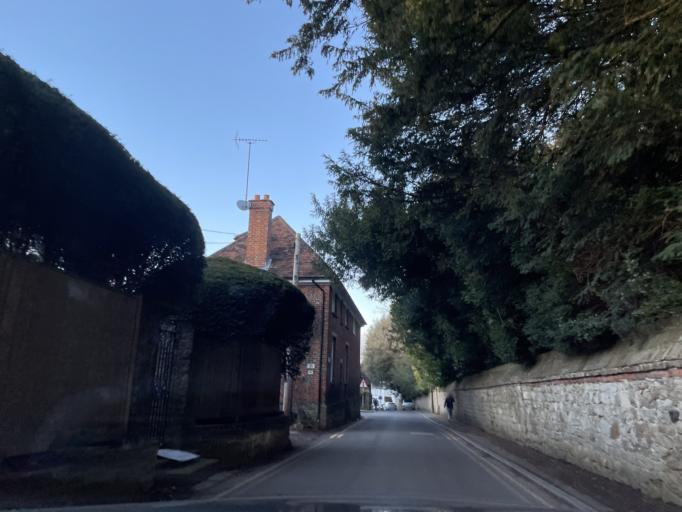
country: GB
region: England
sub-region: Kent
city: Halstead
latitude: 51.2766
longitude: 0.1275
